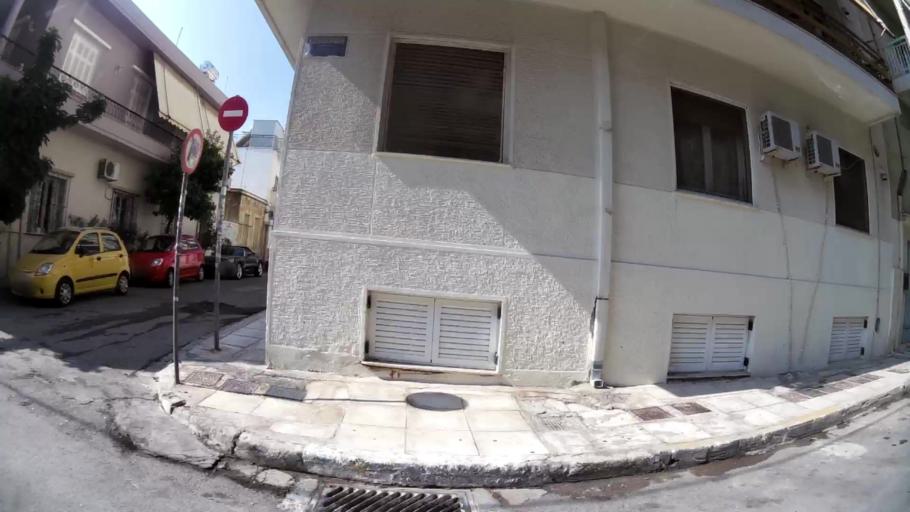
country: GR
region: Attica
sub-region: Nomos Piraios
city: Keratsini
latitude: 37.9612
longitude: 23.6285
